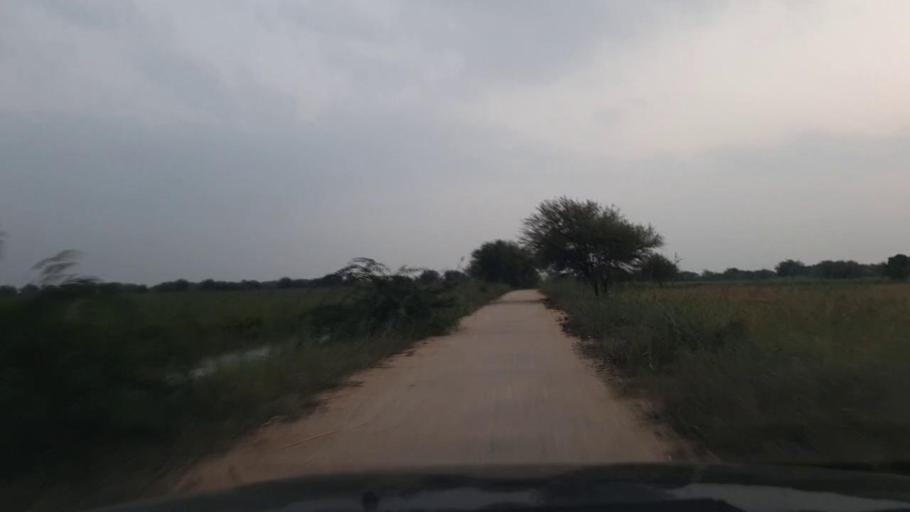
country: PK
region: Sindh
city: Jati
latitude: 24.5205
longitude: 68.3693
